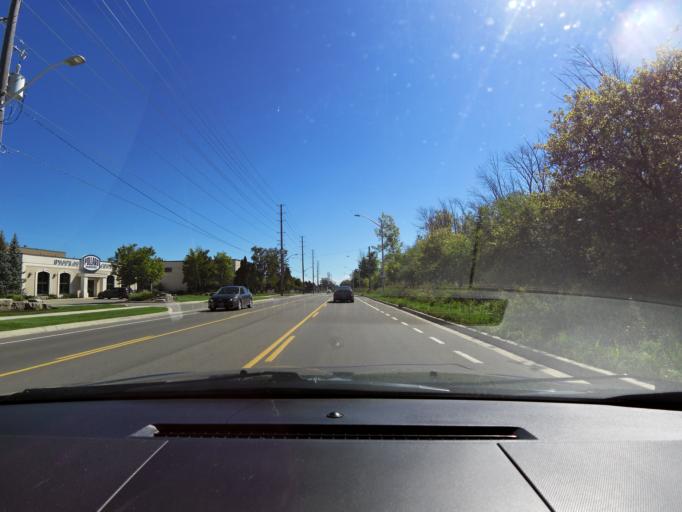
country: CA
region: Ontario
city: Burlington
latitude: 43.3269
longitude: -79.8398
